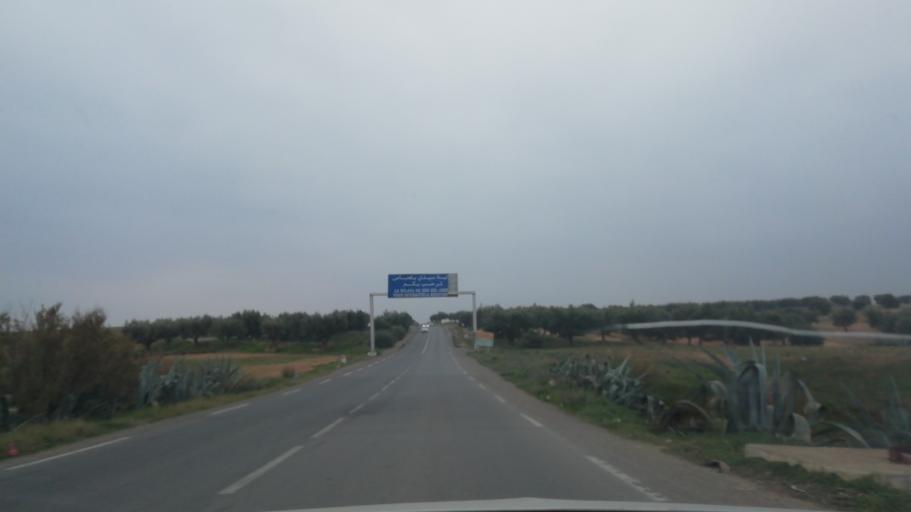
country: DZ
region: Mascara
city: Bou Hanifia el Hamamat
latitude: 35.2814
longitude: -0.1495
